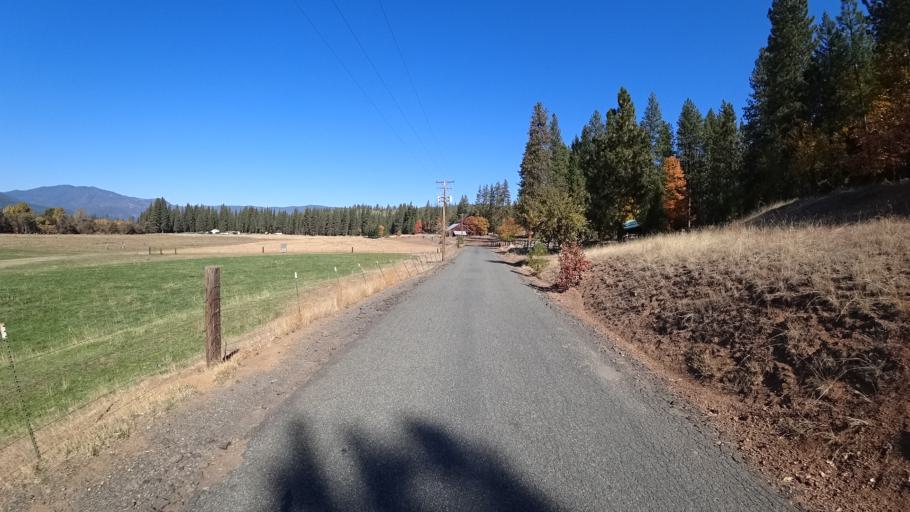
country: US
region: California
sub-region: Siskiyou County
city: Yreka
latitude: 41.5850
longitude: -122.9575
